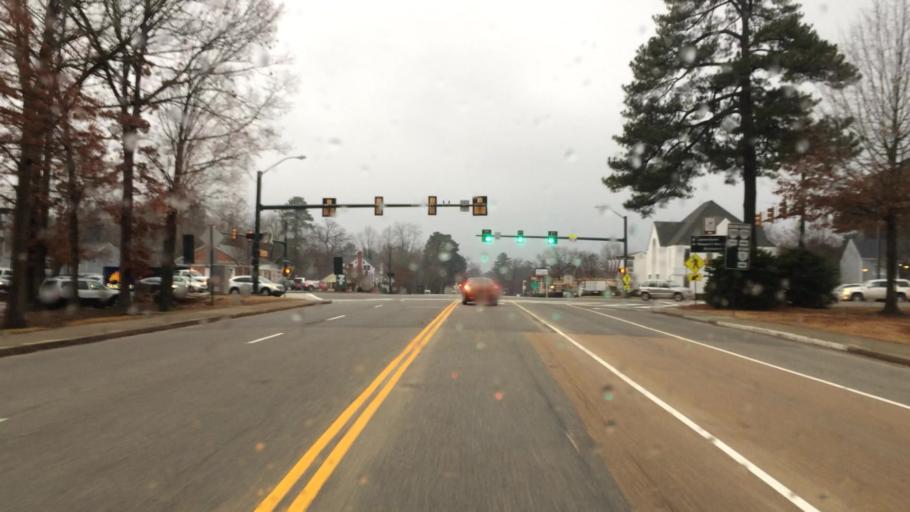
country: US
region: Virginia
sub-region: James City County
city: Williamsburg
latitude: 37.2548
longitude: -76.7311
